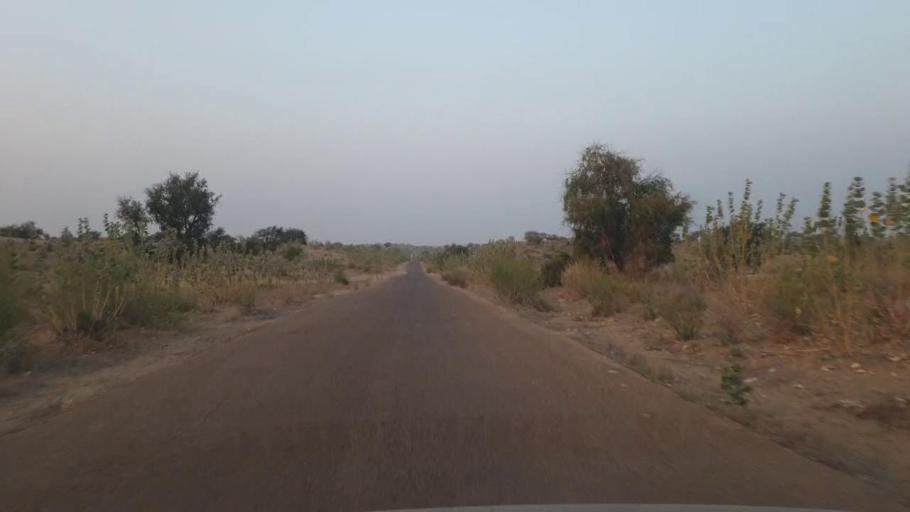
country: PK
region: Sindh
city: Umarkot
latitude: 25.3250
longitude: 70.0576
